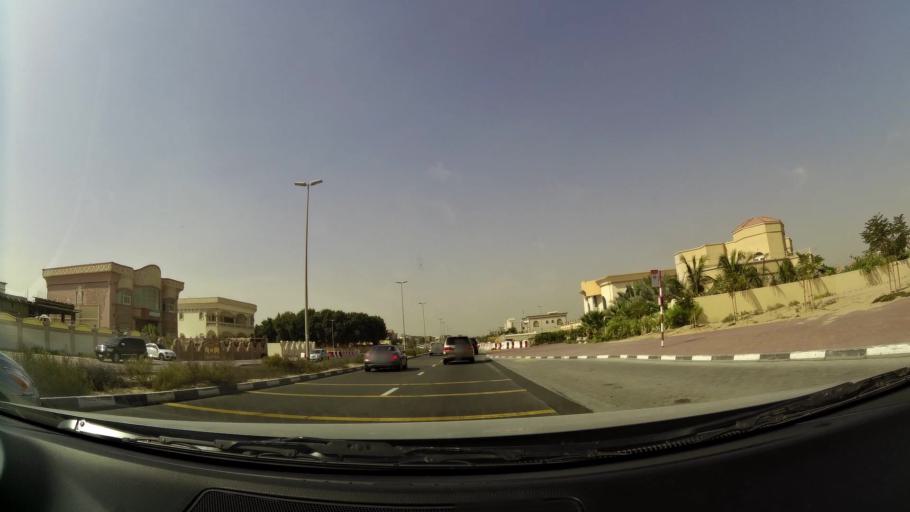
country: AE
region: Ash Shariqah
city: Sharjah
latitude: 25.2045
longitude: 55.4195
